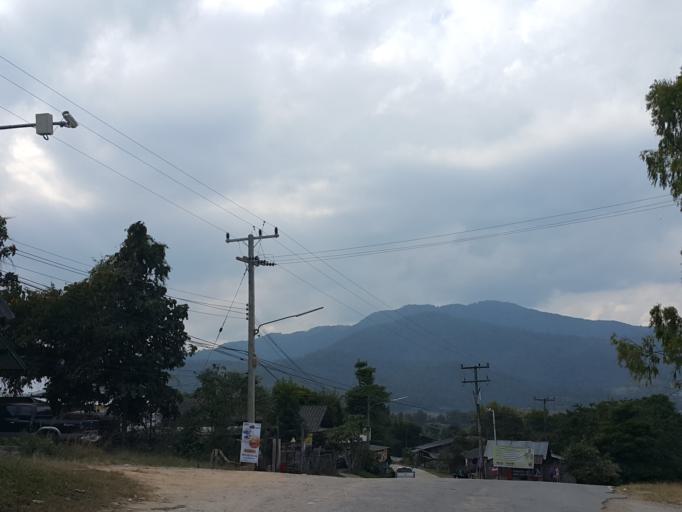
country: TH
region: Chiang Mai
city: Om Koi
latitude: 17.8000
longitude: 98.3385
